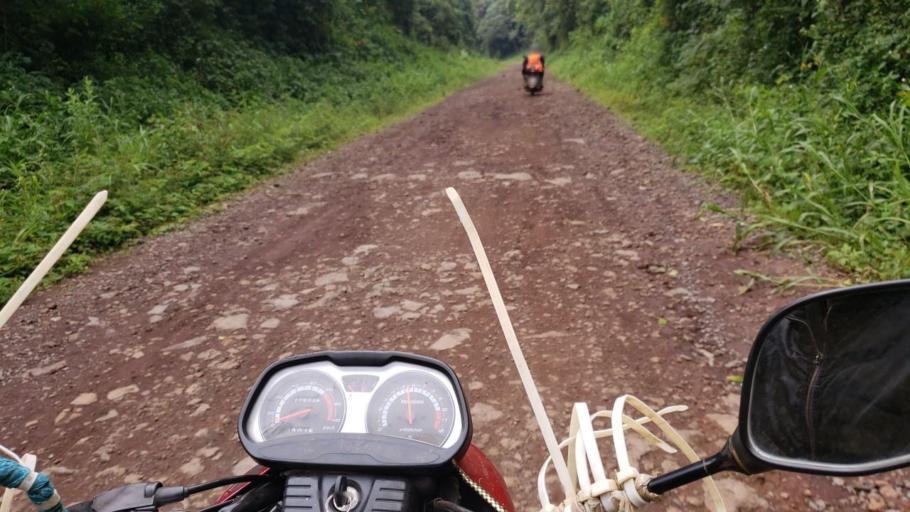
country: CD
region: South Kivu
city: Kabare
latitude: -2.3107
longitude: 28.7506
